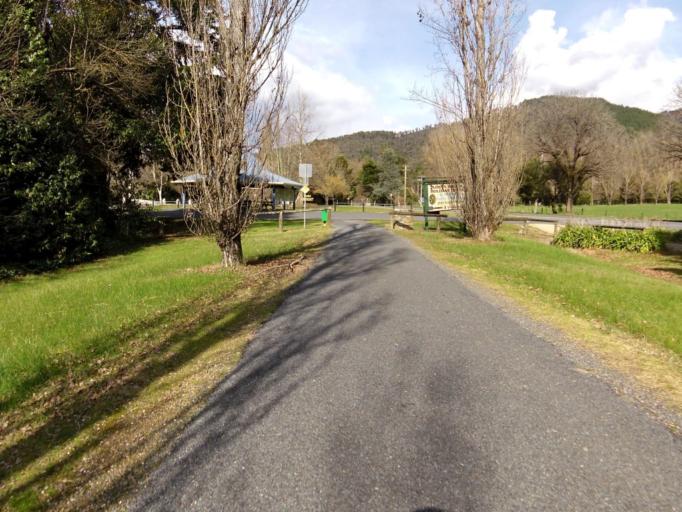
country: AU
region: Victoria
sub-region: Alpine
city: Mount Beauty
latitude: -36.7228
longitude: 146.9461
